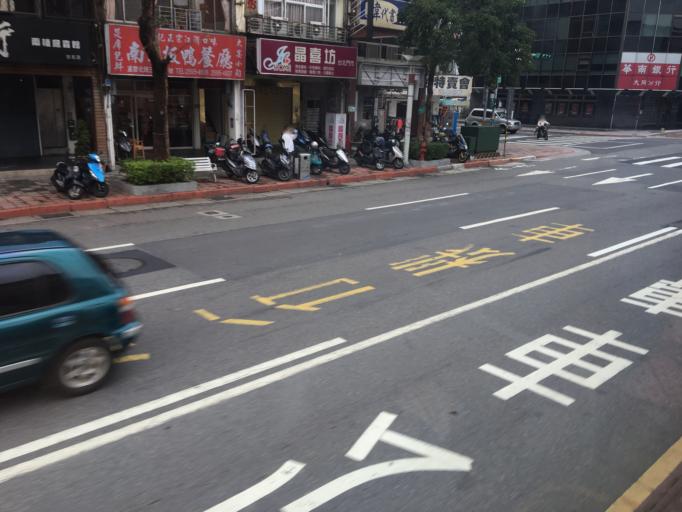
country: TW
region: Taipei
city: Taipei
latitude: 25.0717
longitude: 121.5138
